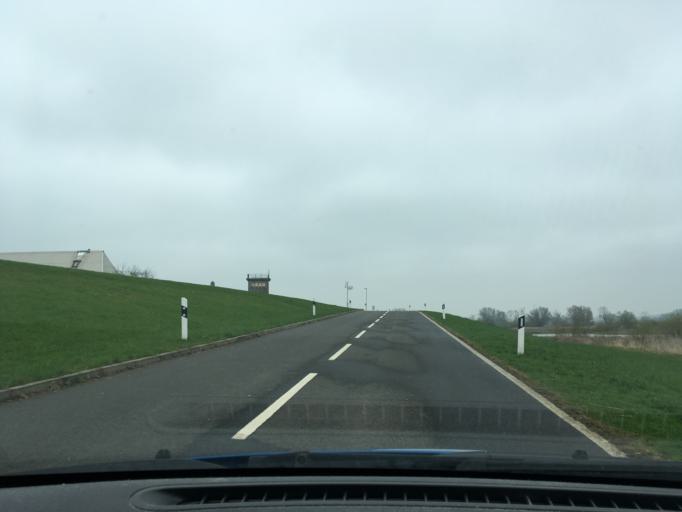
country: DE
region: Lower Saxony
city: Bleckede
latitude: 53.3003
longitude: 10.7428
